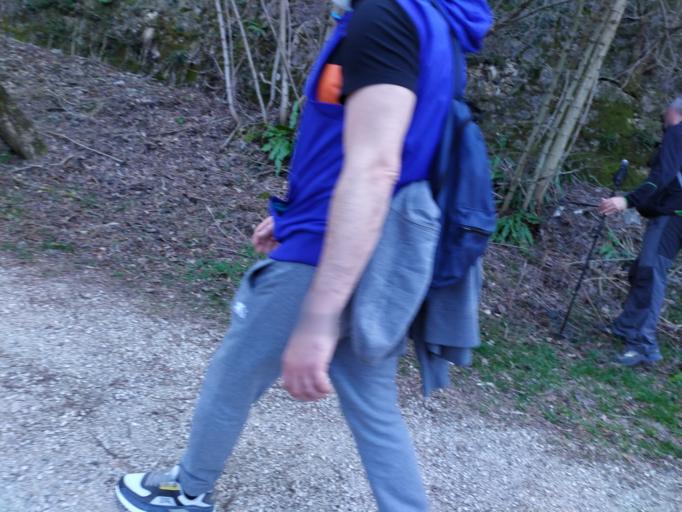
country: IT
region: Veneto
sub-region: Provincia di Vicenza
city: Cogollo del Cengio
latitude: 45.7744
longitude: 11.4108
